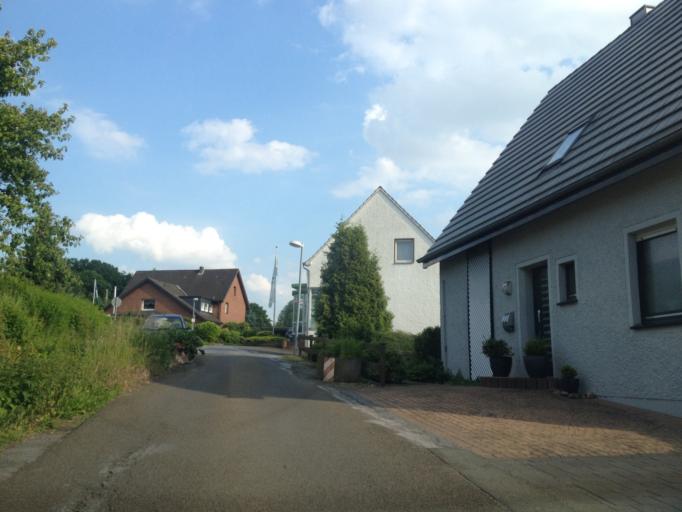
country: DE
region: North Rhine-Westphalia
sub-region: Regierungsbezirk Detmold
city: Rodinghausen
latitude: 52.2551
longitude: 8.5195
